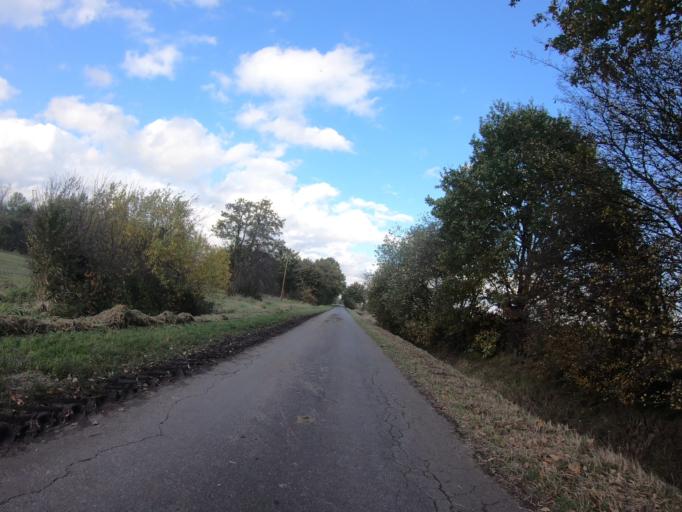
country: DE
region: Lower Saxony
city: Wagenhoff
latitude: 52.5300
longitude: 10.5446
